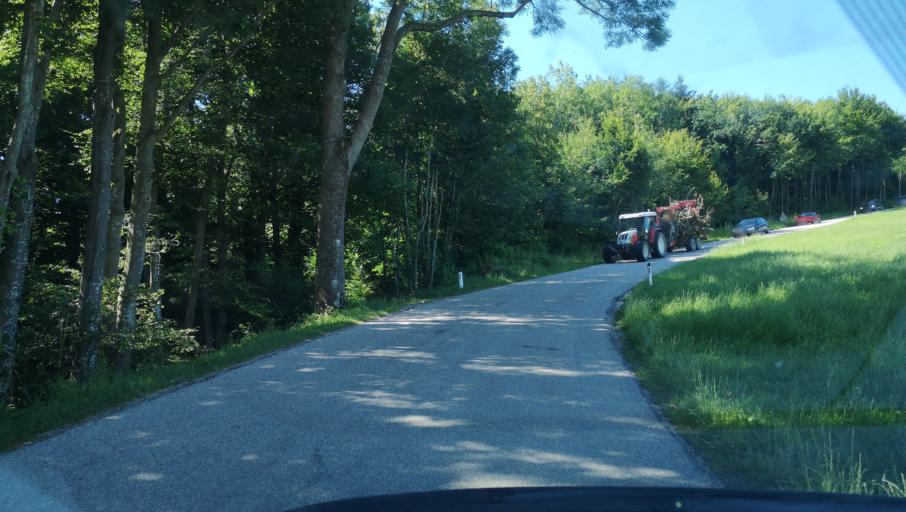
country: AT
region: Lower Austria
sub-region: Politischer Bezirk Amstetten
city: Euratsfeld
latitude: 48.0595
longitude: 14.9174
